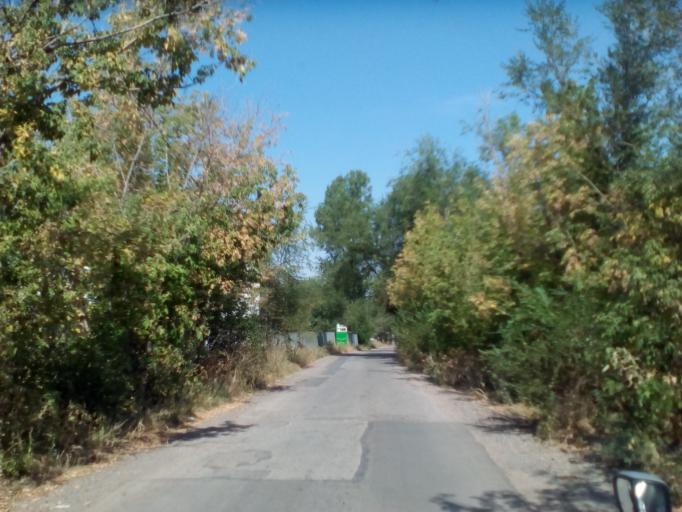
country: KZ
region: Almaty Oblysy
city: Burunday
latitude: 43.1628
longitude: 76.3869
